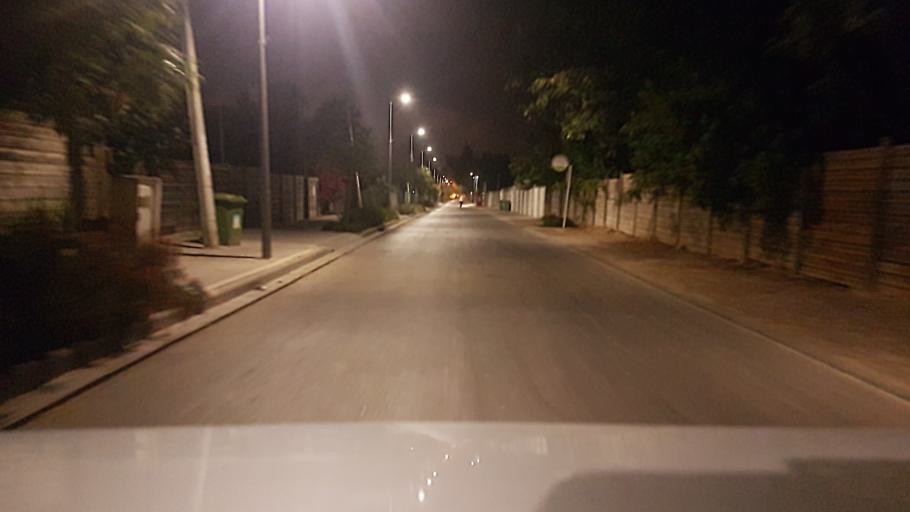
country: IL
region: Central District
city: Nehalim
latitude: 32.0785
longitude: 34.9222
